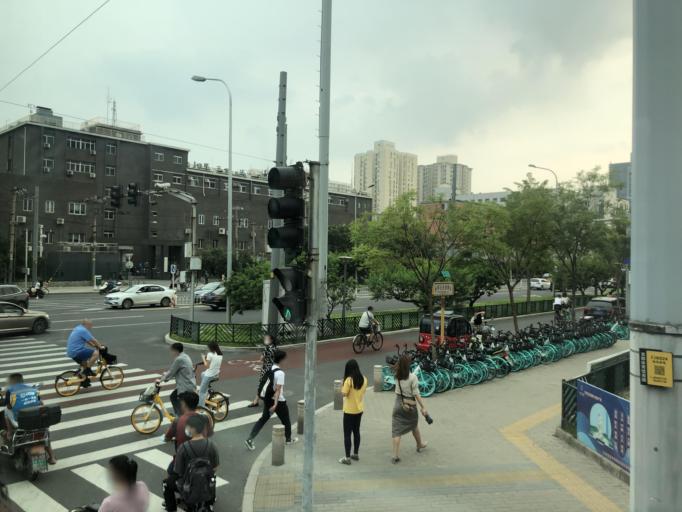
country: CN
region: Beijing
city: Jinrongjie
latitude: 39.9313
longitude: 116.3192
